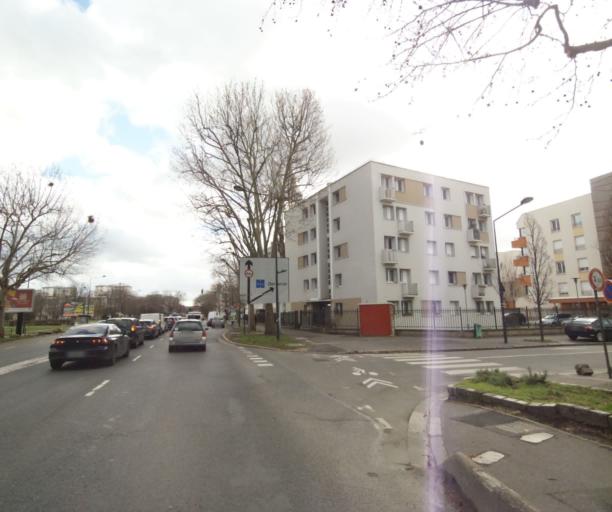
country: FR
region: Ile-de-France
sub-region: Departement de Seine-Saint-Denis
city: Saint-Denis
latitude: 48.9402
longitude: 2.3679
